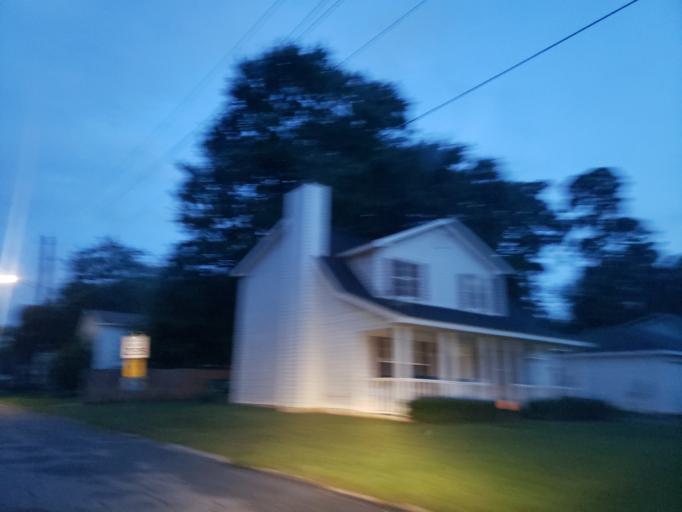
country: US
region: Georgia
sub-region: Chatham County
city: Isle of Hope
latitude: 31.9941
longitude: -81.0734
